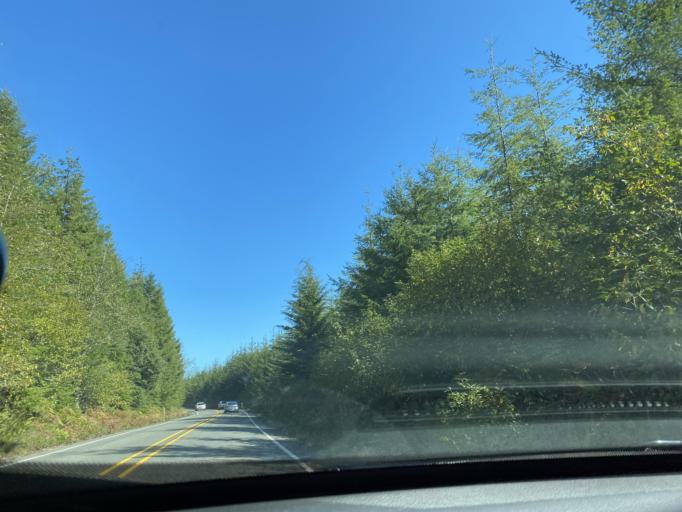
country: US
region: Washington
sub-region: Clallam County
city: Forks
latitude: 47.9357
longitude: -124.4722
